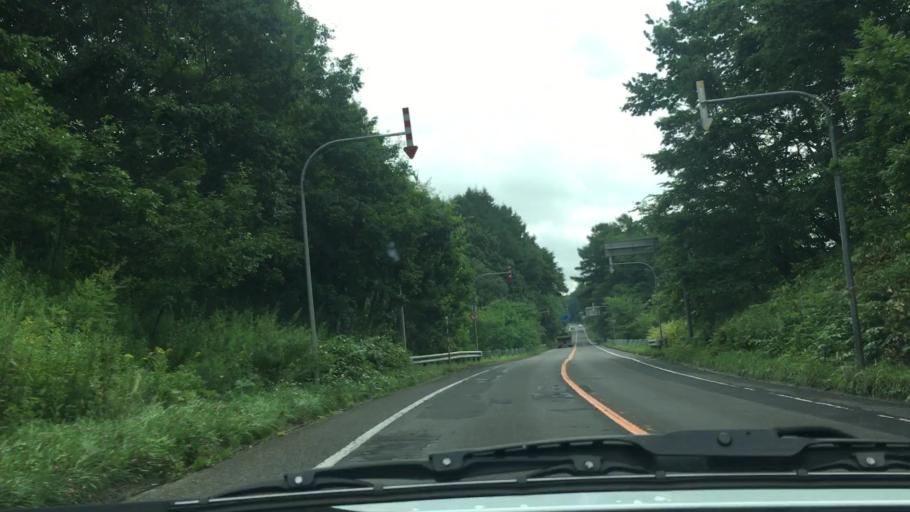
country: JP
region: Hokkaido
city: Chitose
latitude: 42.9453
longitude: 141.7399
